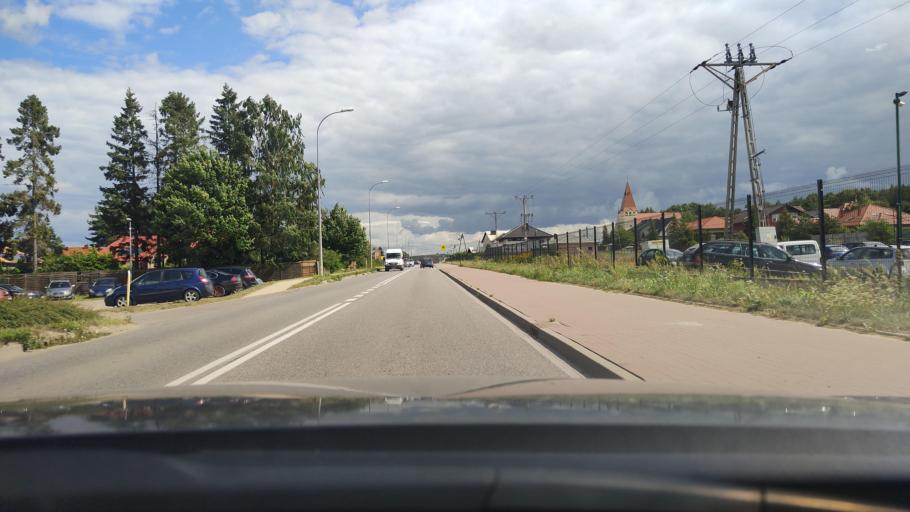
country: PL
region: Pomeranian Voivodeship
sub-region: Powiat wejherowski
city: Bojano
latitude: 54.4756
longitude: 18.3740
